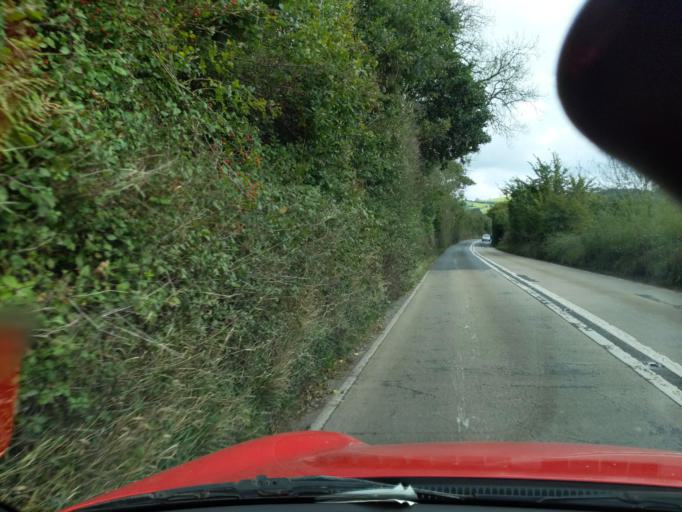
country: GB
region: England
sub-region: Devon
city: Modbury
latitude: 50.3460
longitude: -3.8885
